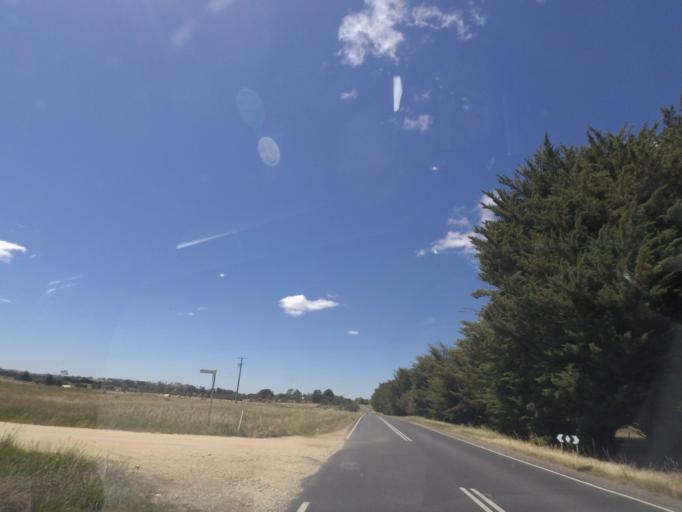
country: AU
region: Victoria
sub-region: Mount Alexander
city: Castlemaine
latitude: -37.2445
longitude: 144.3239
